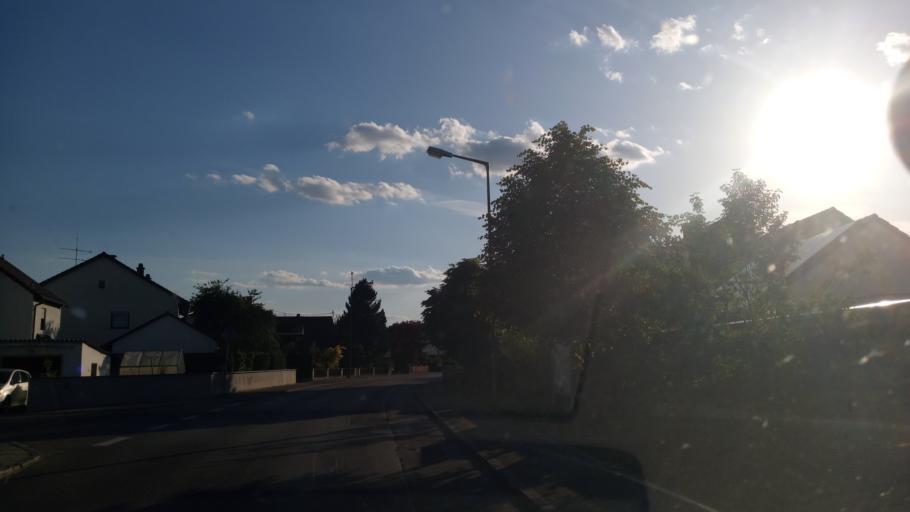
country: DE
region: Bavaria
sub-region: Upper Bavaria
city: Weichs
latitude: 48.3813
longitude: 11.4197
